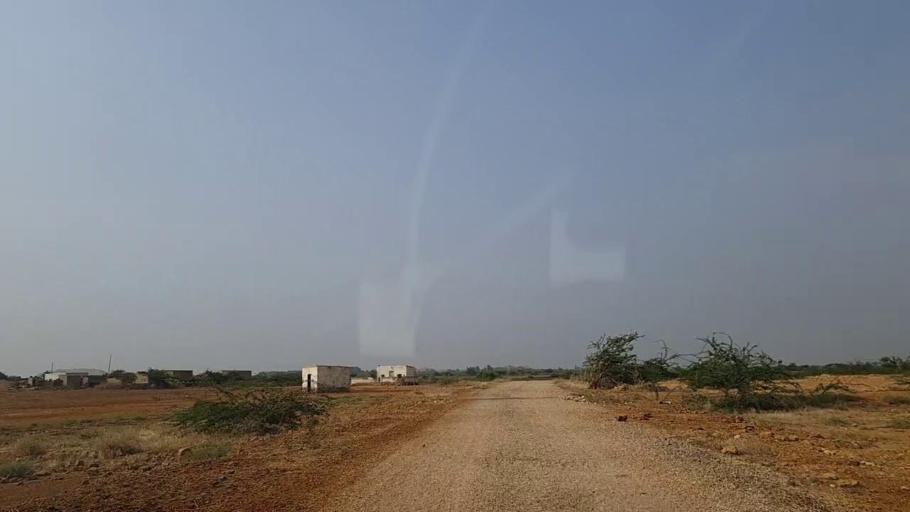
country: PK
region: Sindh
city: Thatta
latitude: 24.7205
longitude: 67.8258
